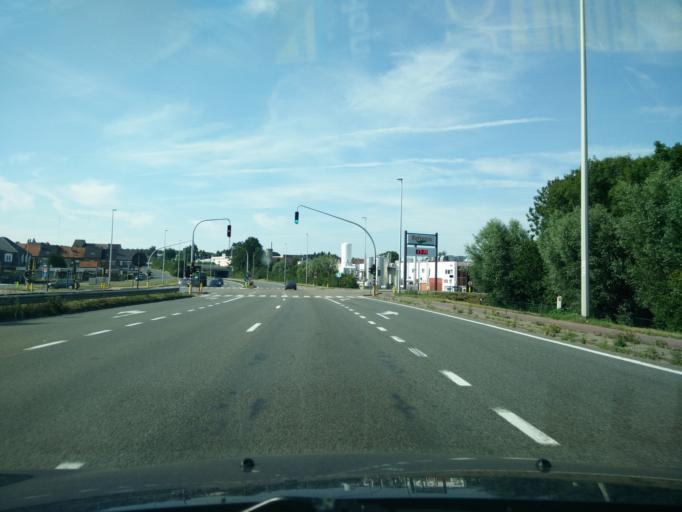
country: BE
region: Flanders
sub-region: Provincie Oost-Vlaanderen
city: Ninove
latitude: 50.8382
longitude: 4.0382
